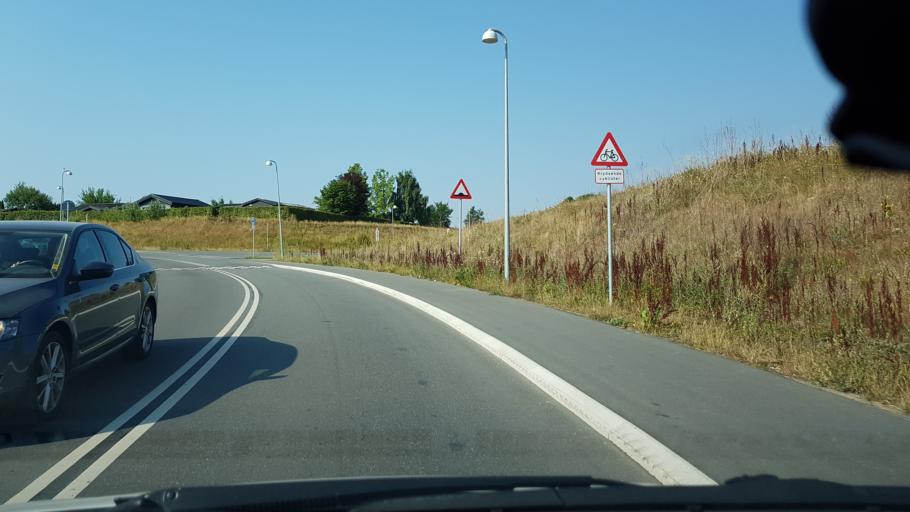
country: DK
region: Capital Region
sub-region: Brondby Kommune
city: Brondbyvester
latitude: 55.6412
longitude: 12.3905
